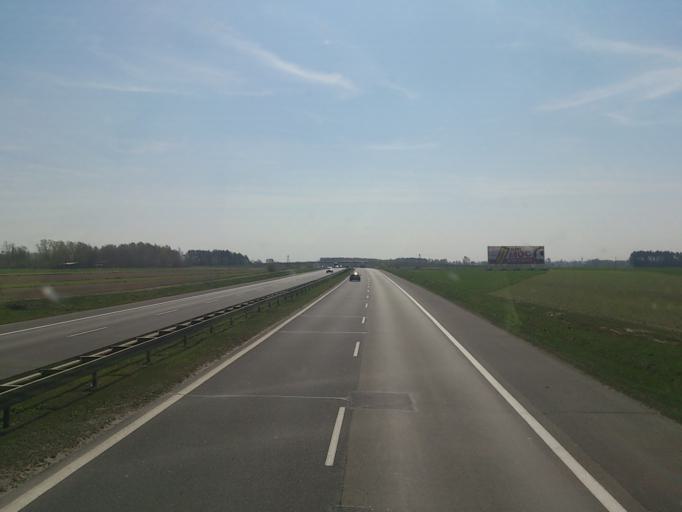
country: PL
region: Lodz Voivodeship
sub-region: Powiat piotrkowski
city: Grabica
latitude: 51.5048
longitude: 19.6043
